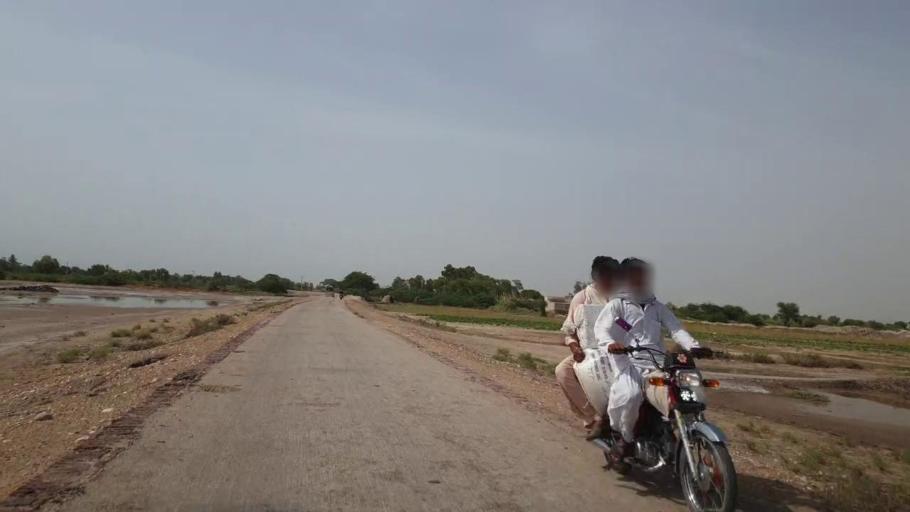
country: PK
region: Sindh
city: Bandhi
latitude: 26.5670
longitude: 68.3805
